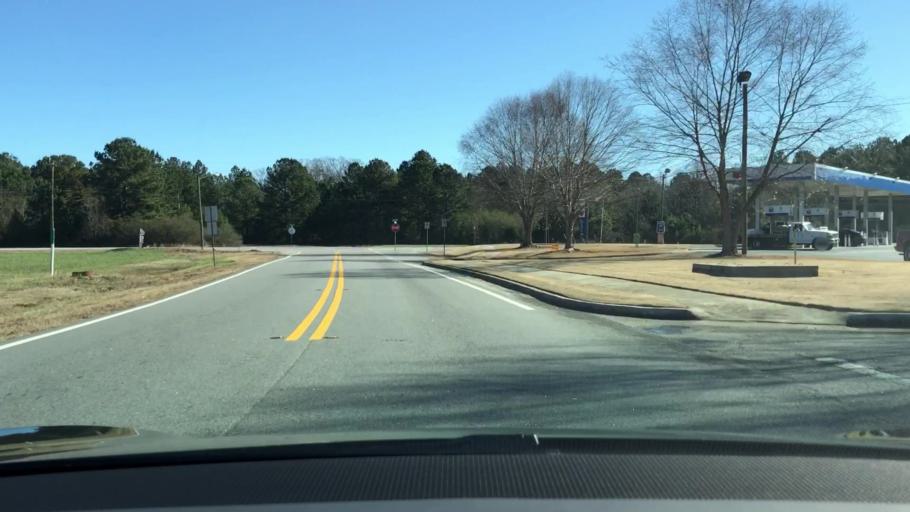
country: US
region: Georgia
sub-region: Walton County
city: Monroe
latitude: 33.8332
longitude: -83.7330
